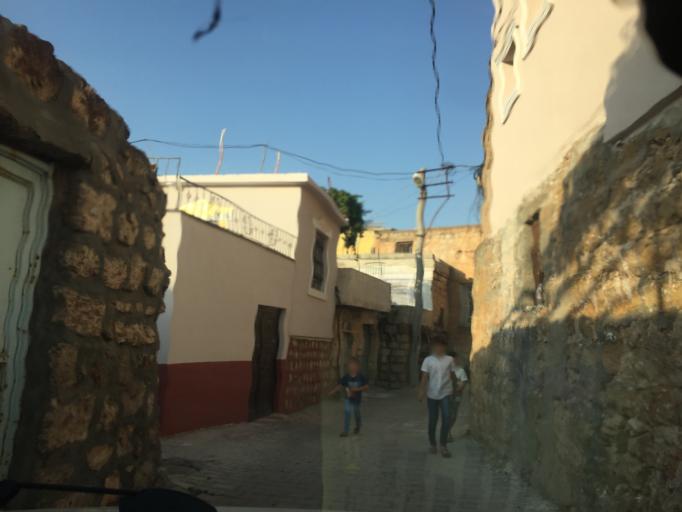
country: TR
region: Mardin
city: Kindirip
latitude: 37.4458
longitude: 41.2186
